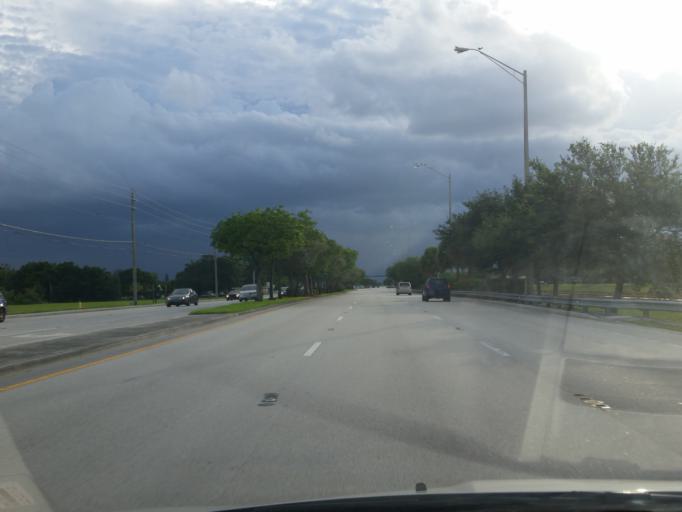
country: US
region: Florida
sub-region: Broward County
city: Davie
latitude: 26.0653
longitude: -80.2242
